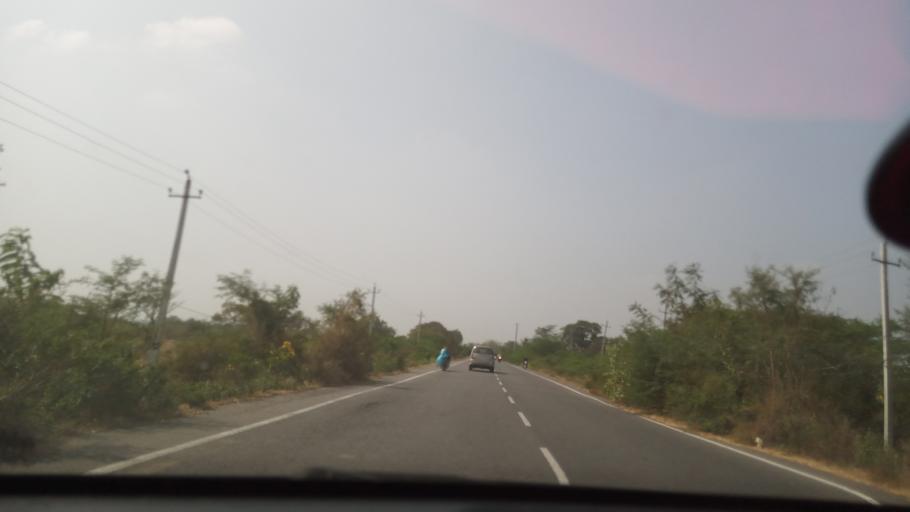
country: IN
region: Karnataka
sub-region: Mysore
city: Nanjangud
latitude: 12.0600
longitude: 76.7631
